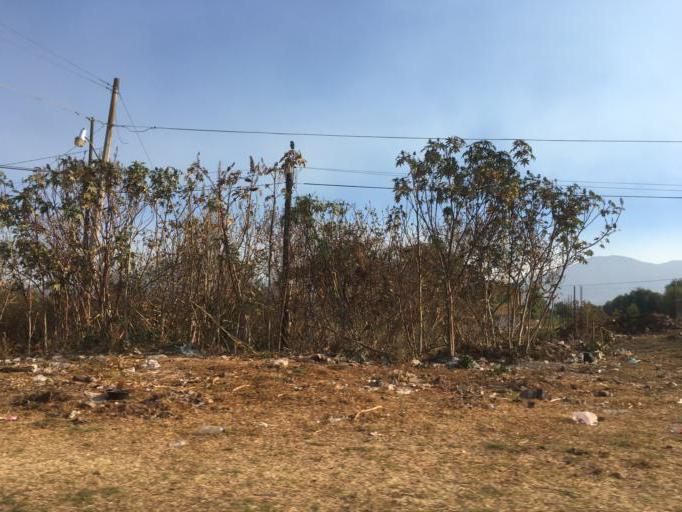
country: MX
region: Michoacan
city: Santa Fe de la Laguna
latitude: 19.6696
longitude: -101.5522
